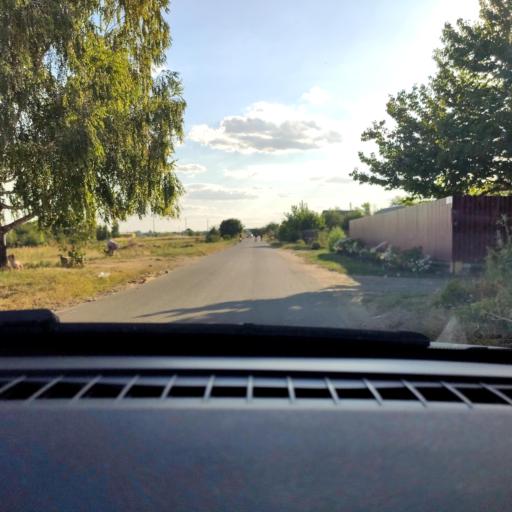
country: RU
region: Voronezj
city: Devitsa
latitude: 51.6464
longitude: 38.9469
